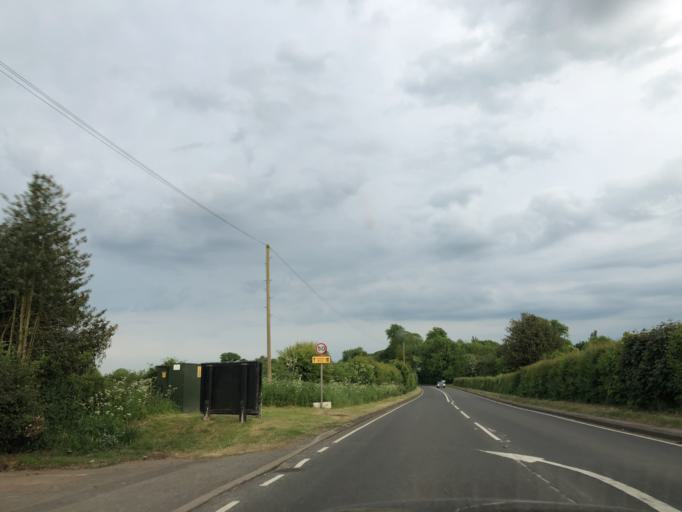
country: GB
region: England
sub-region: Warwickshire
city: Wroxall
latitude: 52.3091
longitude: -1.6624
